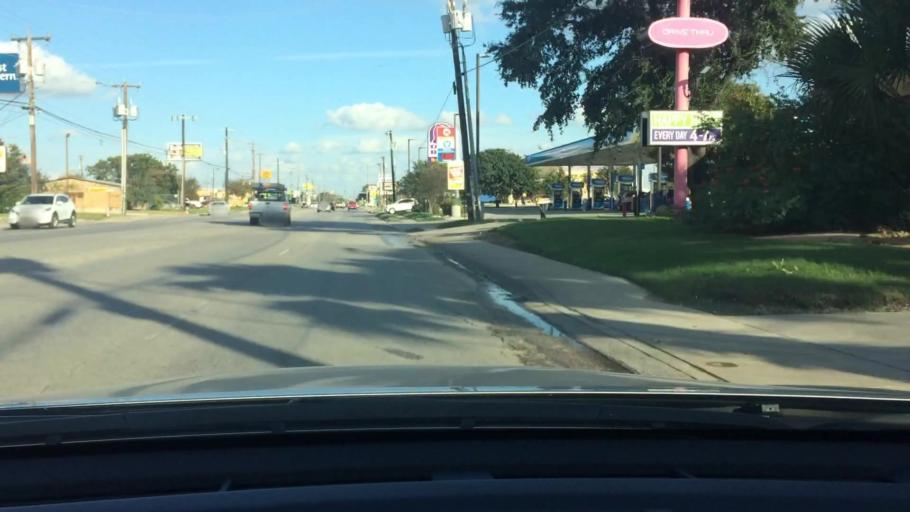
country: US
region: Texas
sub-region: Bexar County
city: Kirby
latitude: 29.4840
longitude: -98.4008
